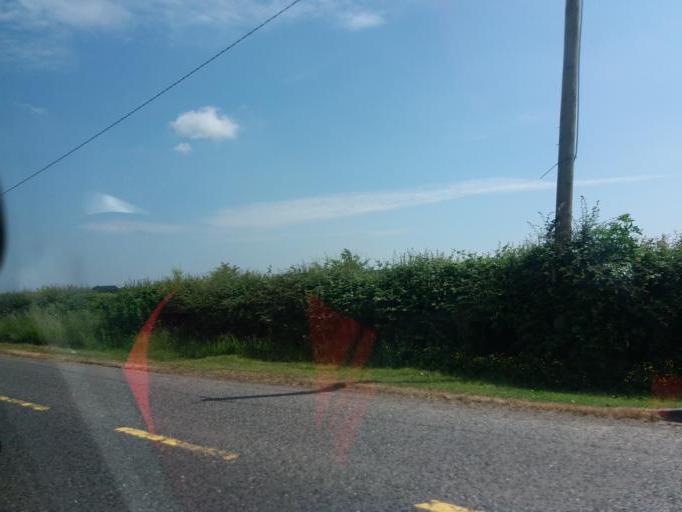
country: IE
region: Leinster
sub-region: An Mhi
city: Slane
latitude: 53.6999
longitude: -6.5907
